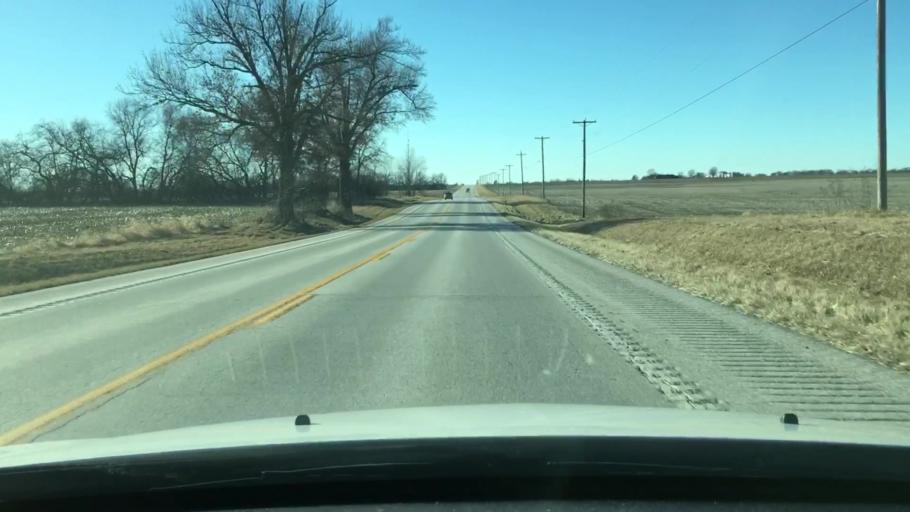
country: US
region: Missouri
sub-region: Pike County
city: Bowling Green
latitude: 39.3445
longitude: -91.2826
